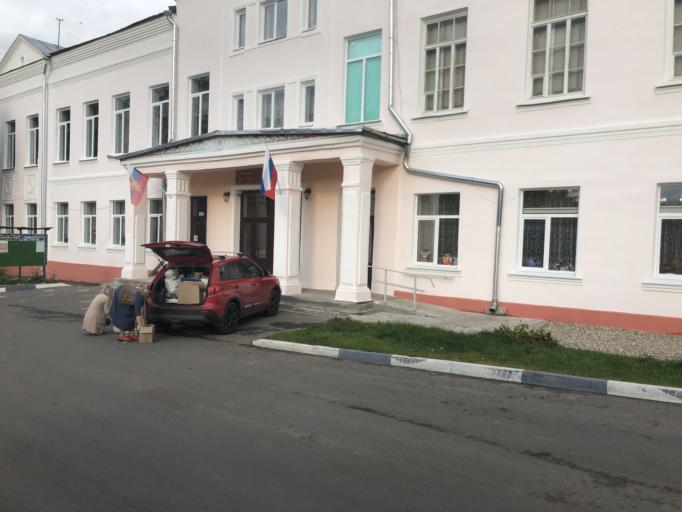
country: RU
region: Tverskaya
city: Rzhev
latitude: 56.2554
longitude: 34.2930
